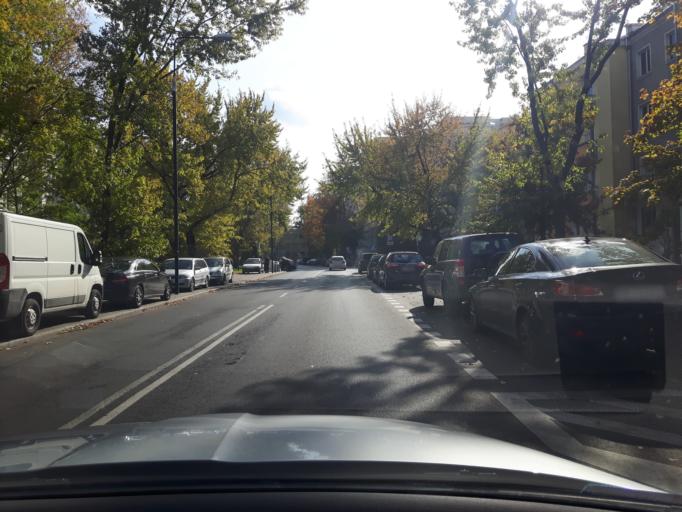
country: PL
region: Masovian Voivodeship
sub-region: Warszawa
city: Wola
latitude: 52.2483
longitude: 20.9959
